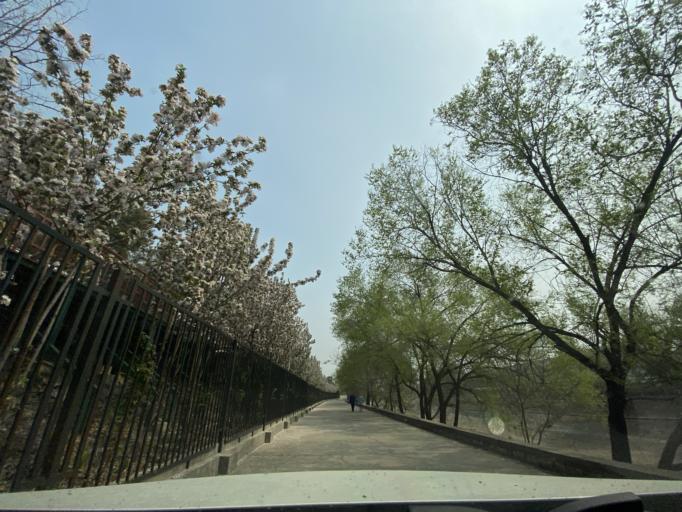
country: CN
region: Beijing
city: Sijiqing
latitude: 39.9398
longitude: 116.2484
